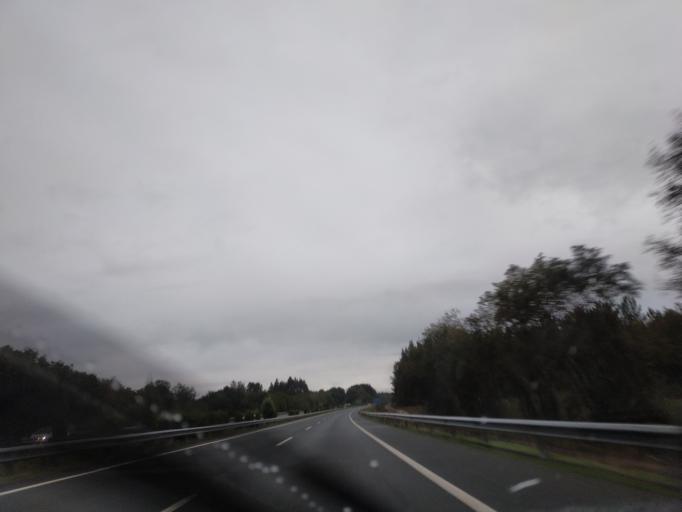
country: ES
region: Galicia
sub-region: Provincia de Lugo
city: Begonte
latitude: 43.1675
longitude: -7.6956
